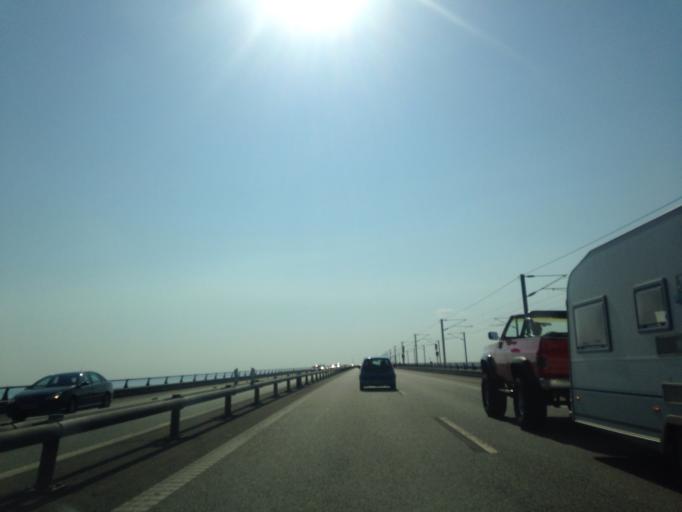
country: DK
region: South Denmark
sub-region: Nyborg Kommune
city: Nyborg
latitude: 55.3250
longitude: 10.9448
